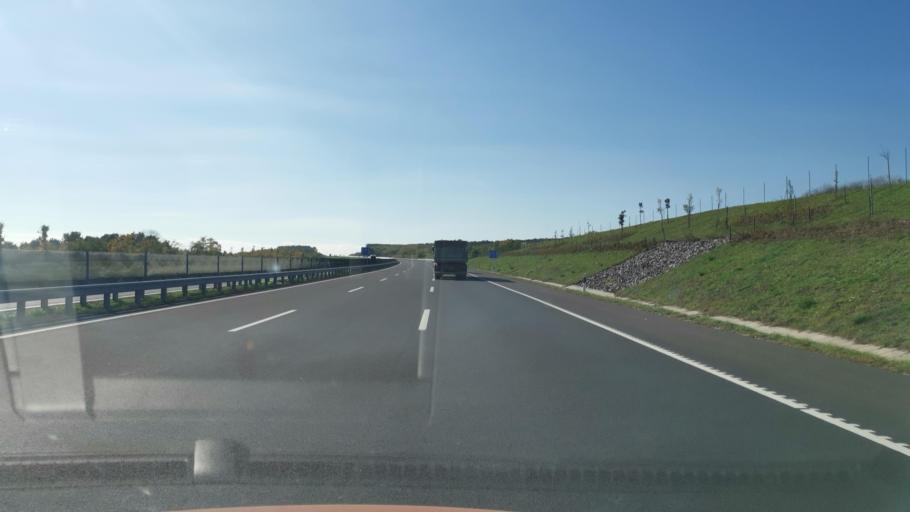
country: HU
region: Borsod-Abauj-Zemplen
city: Aszalo
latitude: 48.2287
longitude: 20.9475
